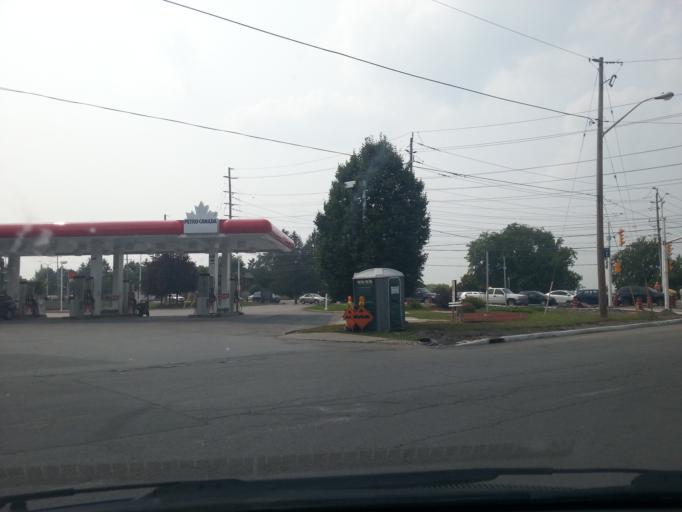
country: CA
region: Ontario
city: Ottawa
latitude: 45.4495
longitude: -75.5879
